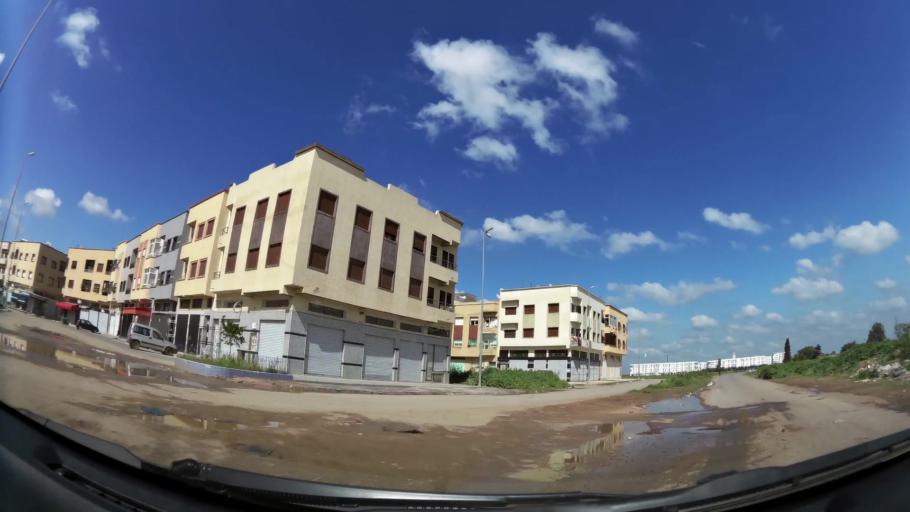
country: MA
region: Grand Casablanca
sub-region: Mediouna
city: Mediouna
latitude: 33.4539
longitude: -7.5076
